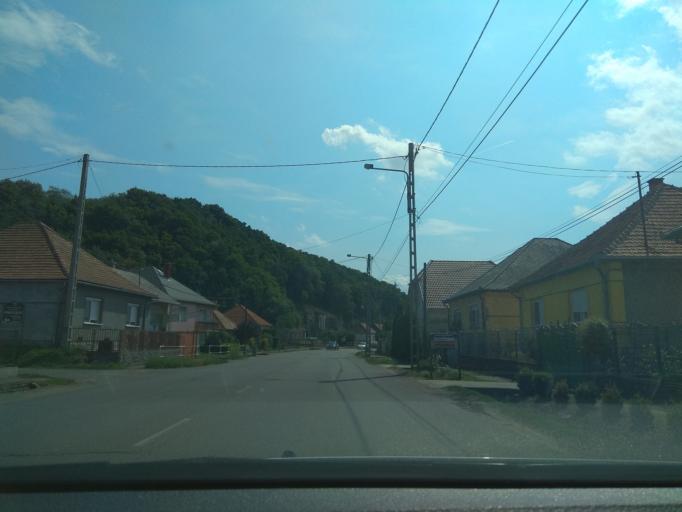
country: HU
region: Heves
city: Andornaktalya
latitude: 47.8518
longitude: 20.4098
